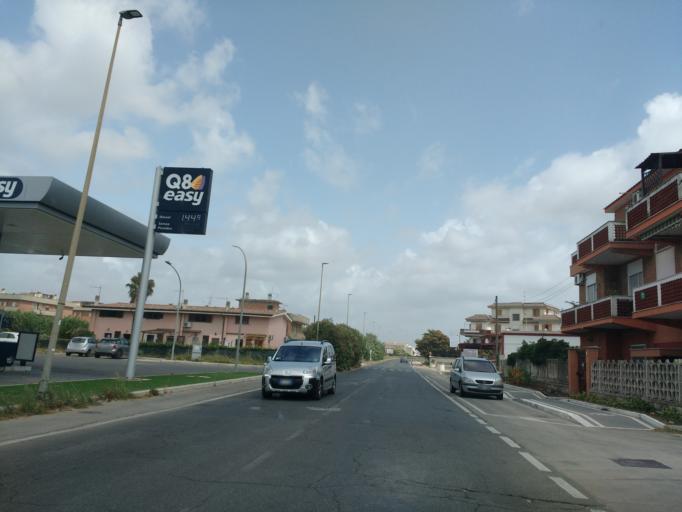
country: IT
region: Latium
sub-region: Citta metropolitana di Roma Capitale
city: Ardea
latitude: 41.5812
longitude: 12.5059
